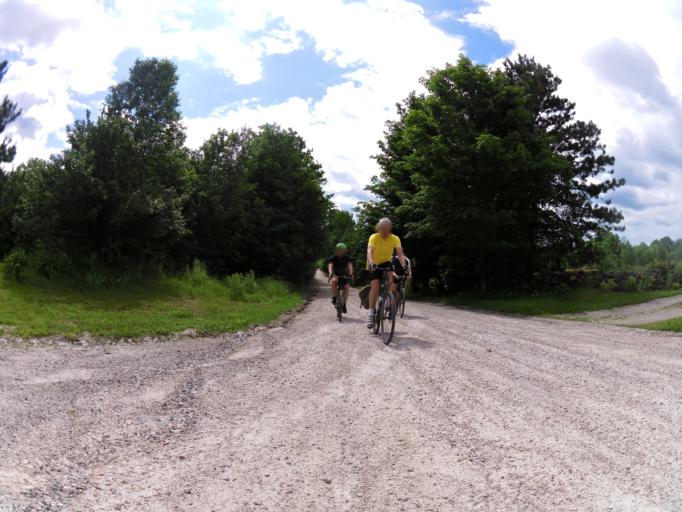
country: CA
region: Ontario
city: Perth
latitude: 45.0277
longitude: -76.5182
